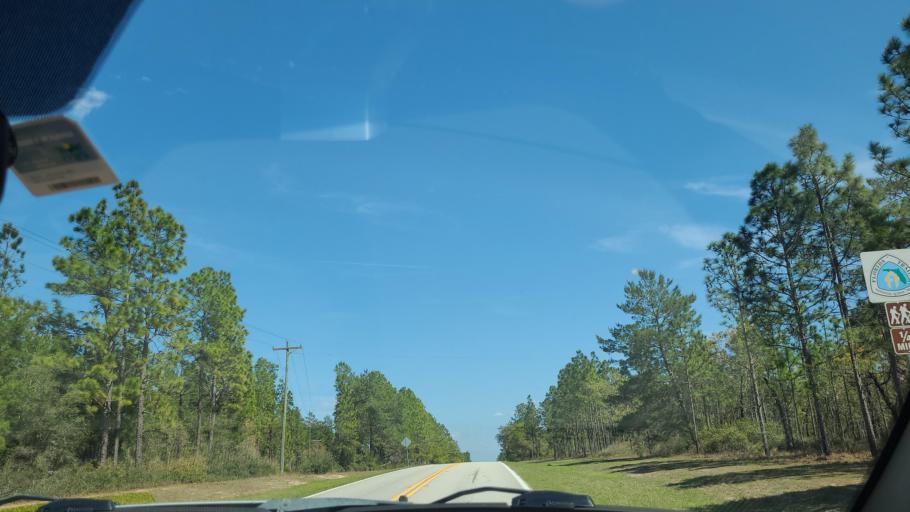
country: US
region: Florida
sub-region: Putnam County
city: Interlachen
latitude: 29.3666
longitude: -81.8269
